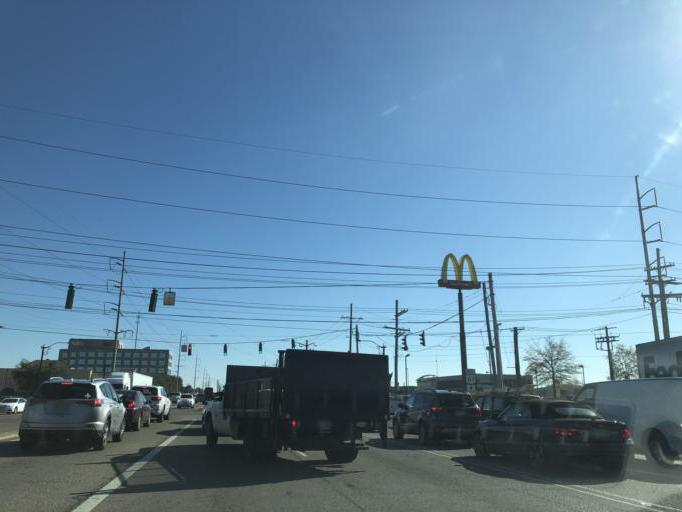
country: US
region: Louisiana
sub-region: Jefferson Parish
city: Jefferson
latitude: 29.9744
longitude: -90.1527
